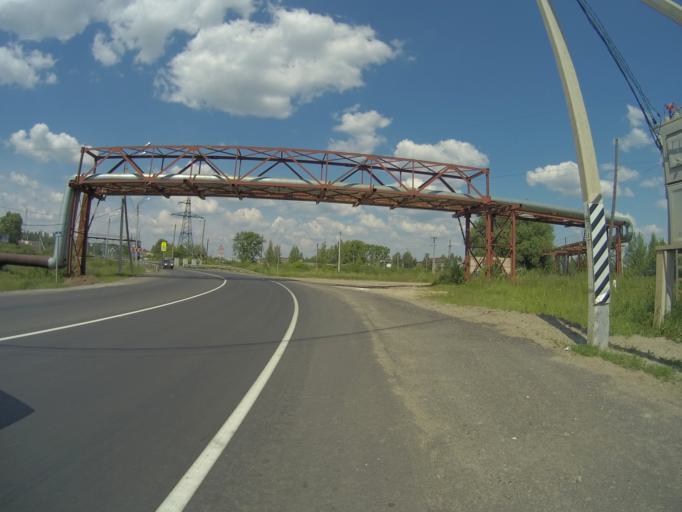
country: RU
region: Kostroma
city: Volgorechensk
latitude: 57.4441
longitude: 41.1662
